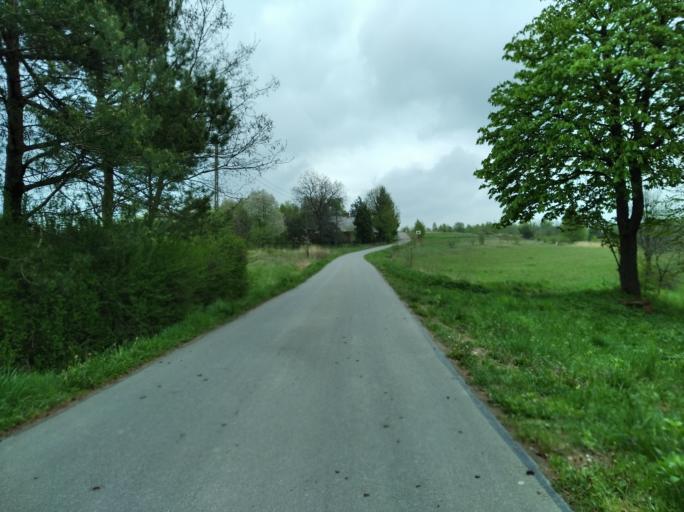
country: PL
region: Subcarpathian Voivodeship
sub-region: Powiat brzozowski
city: Golcowa
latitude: 49.7532
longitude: 22.0414
